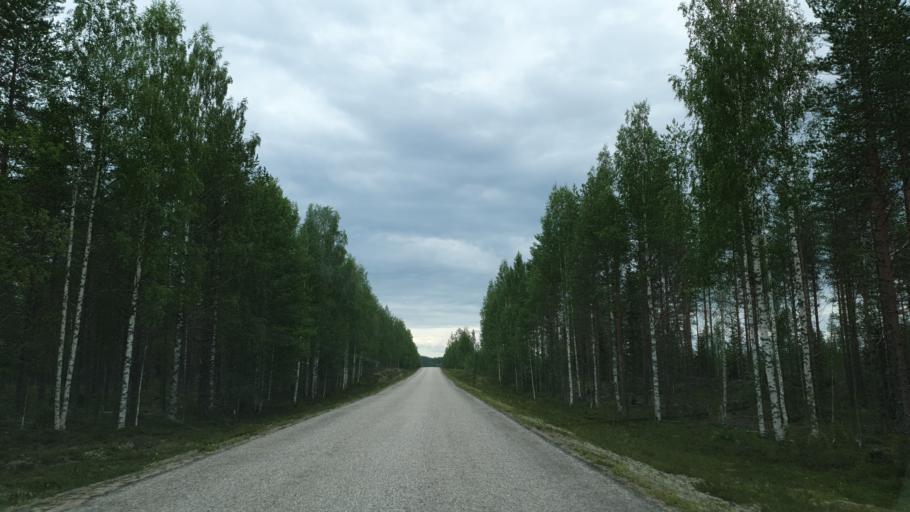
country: FI
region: Kainuu
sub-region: Kehys-Kainuu
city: Kuhmo
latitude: 64.3413
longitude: 29.3088
